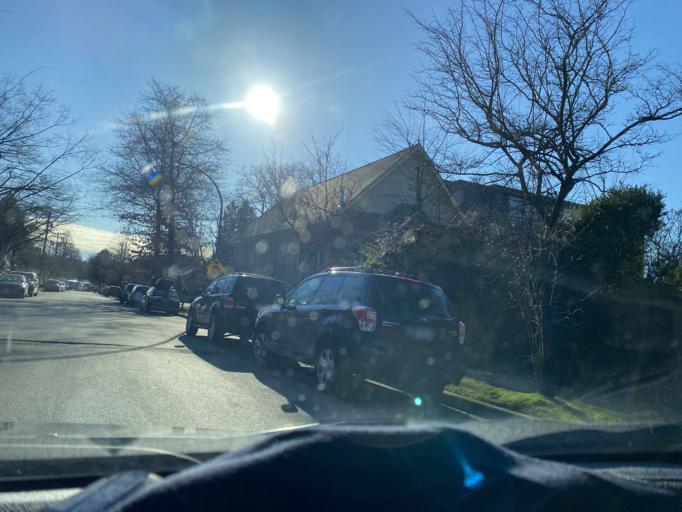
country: CA
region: British Columbia
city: West End
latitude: 49.2664
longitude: -123.1576
